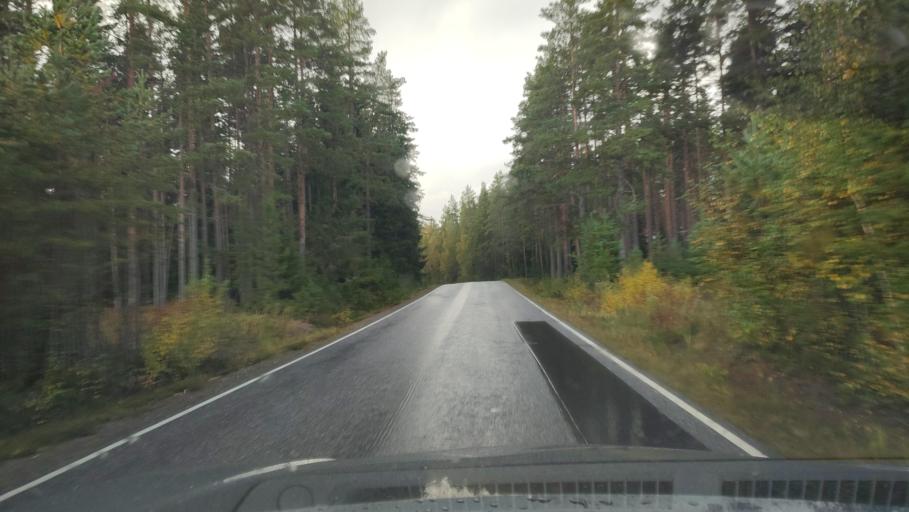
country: FI
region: Southern Ostrobothnia
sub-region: Suupohja
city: Karijoki
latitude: 62.3262
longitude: 21.6701
